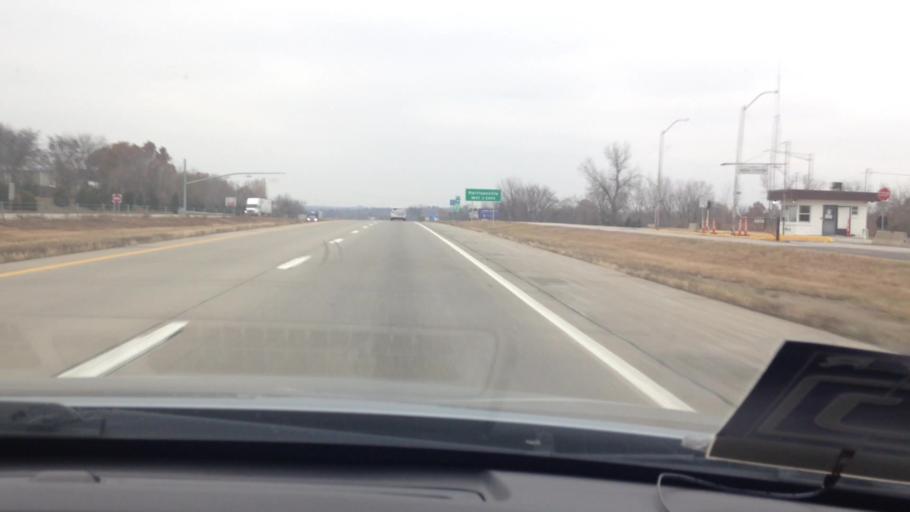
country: US
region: Missouri
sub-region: Cass County
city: Harrisonville
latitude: 38.6275
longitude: -94.3500
